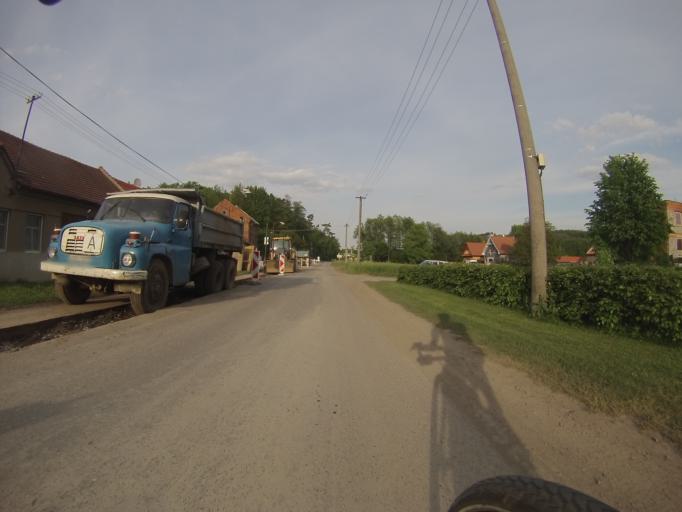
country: CZ
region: Olomoucky
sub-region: Okres Prostejov
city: Plumlov
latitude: 49.4625
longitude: 16.9979
